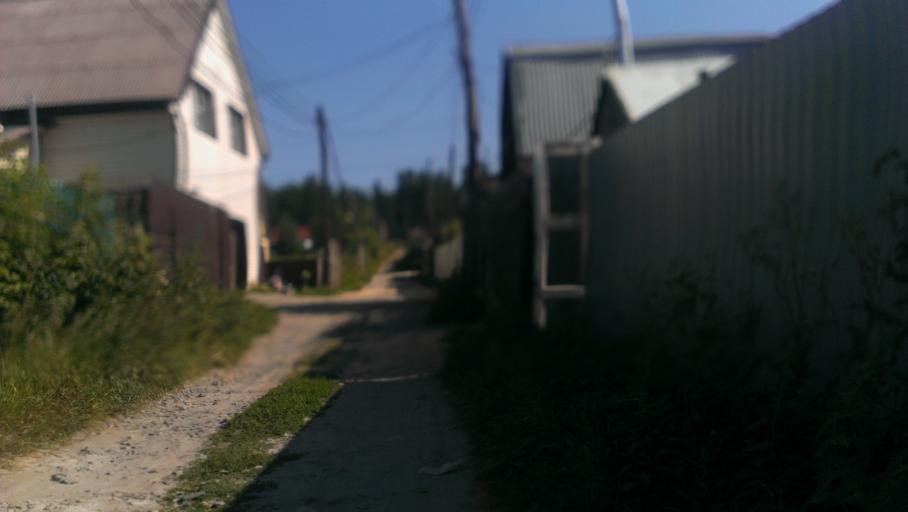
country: RU
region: Altai Krai
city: Novosilikatnyy
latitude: 53.3211
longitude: 83.6841
